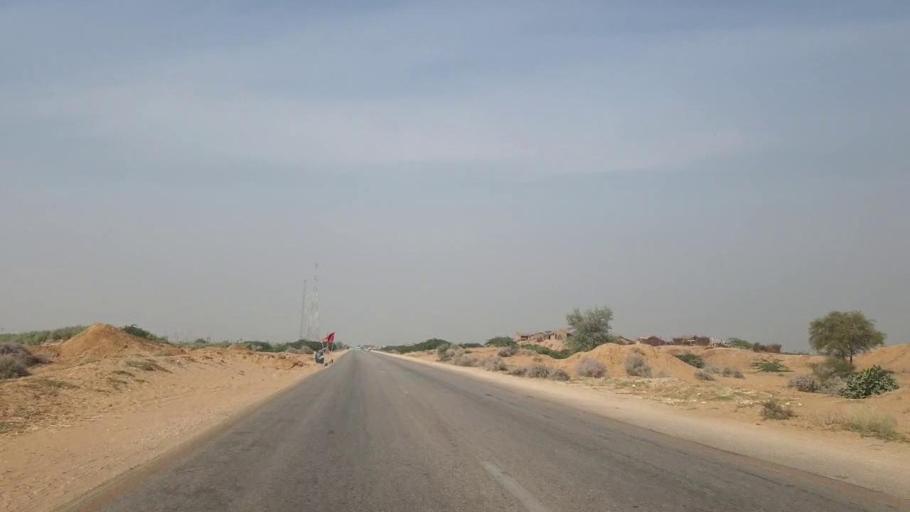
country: PK
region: Sindh
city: Sann
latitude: 26.0486
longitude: 68.1092
